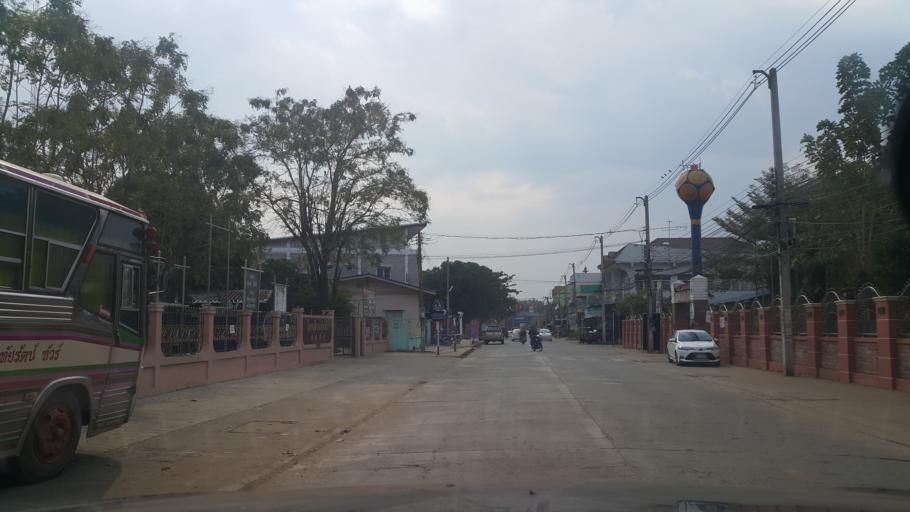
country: TH
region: Sukhothai
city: Si Samrong
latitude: 17.1653
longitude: 99.8606
